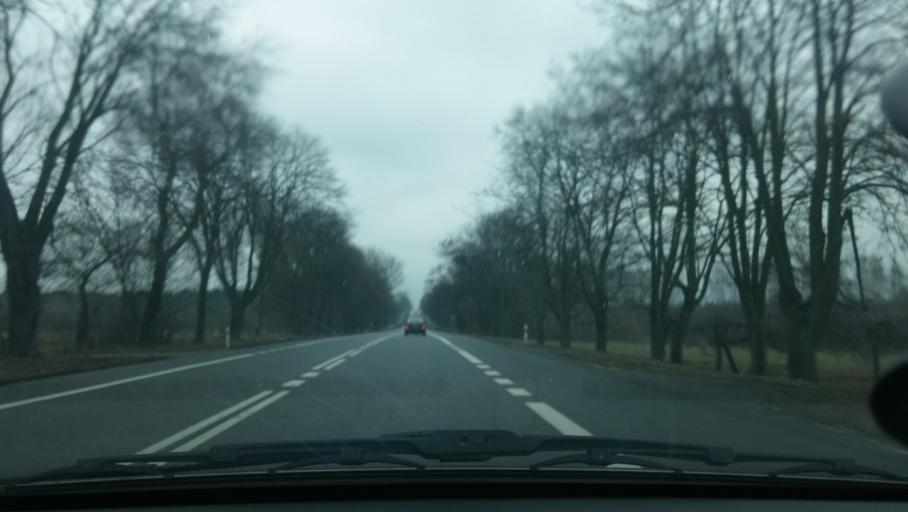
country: PL
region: Masovian Voivodeship
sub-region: Powiat wegrowski
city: Grebkow
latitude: 52.2059
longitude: 21.9322
